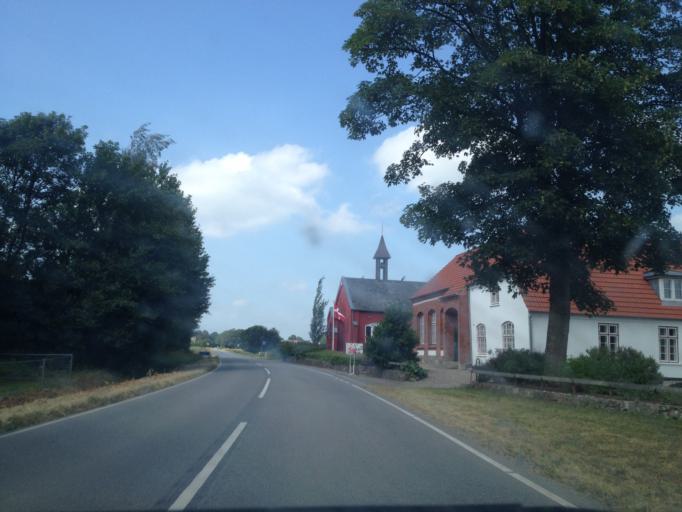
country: DK
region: South Denmark
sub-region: Kolding Kommune
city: Vamdrup
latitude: 55.3776
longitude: 9.2775
